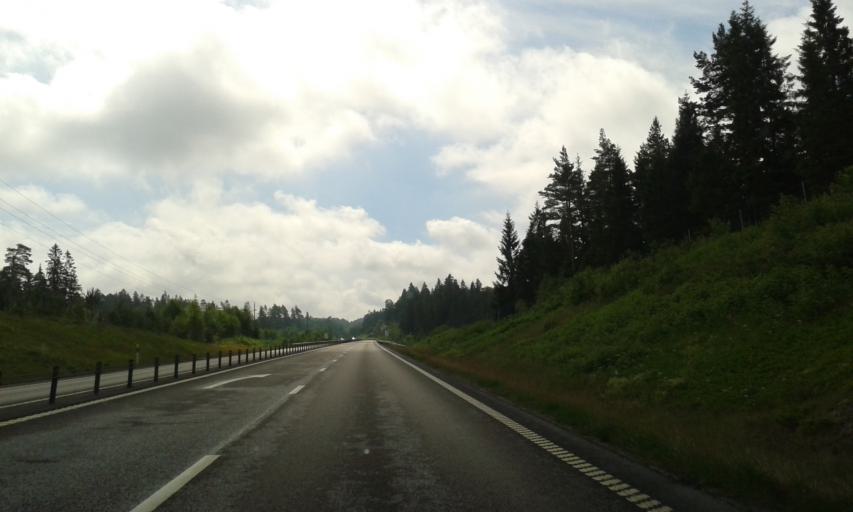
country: SE
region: Vaestra Goetaland
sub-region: Boras Kommun
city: Ganghester
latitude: 57.6641
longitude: 13.0357
